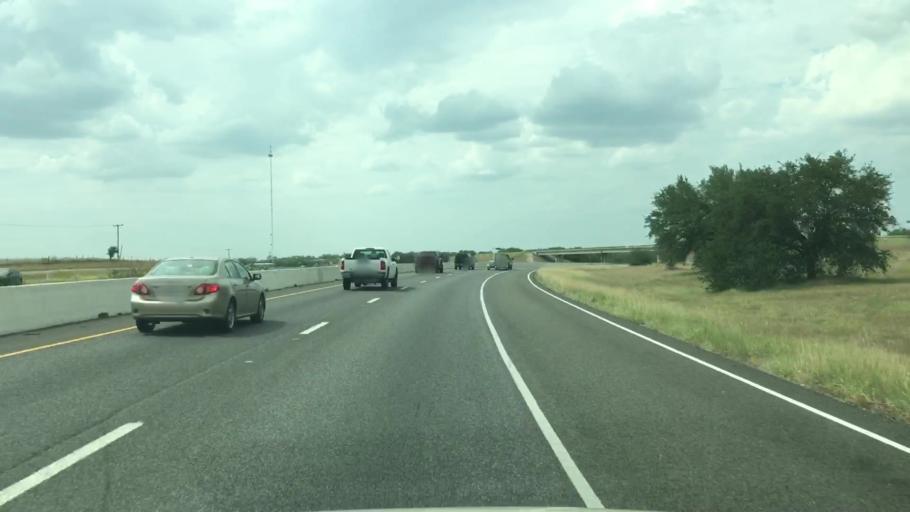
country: US
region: Texas
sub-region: Atascosa County
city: Pleasanton
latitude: 28.9071
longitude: -98.4313
